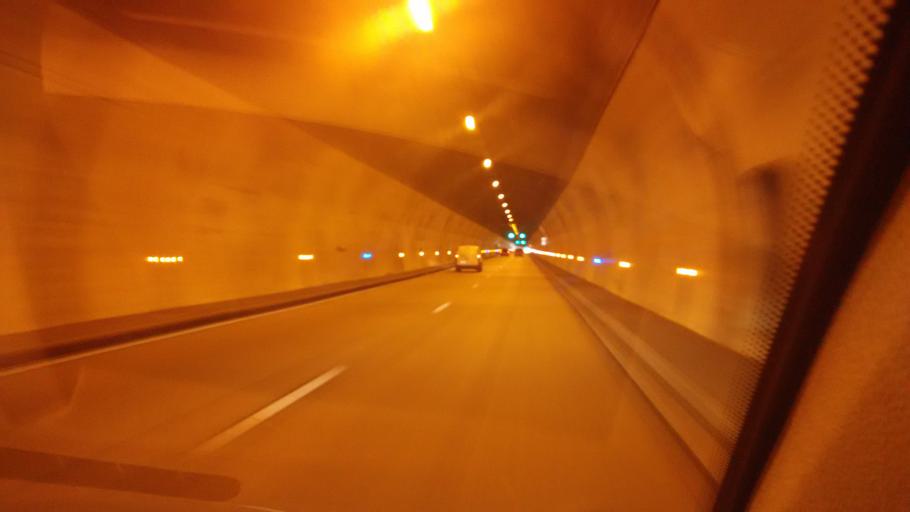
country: FR
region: Provence-Alpes-Cote d'Azur
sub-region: Departement des Alpes-Maritimes
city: Gorbio
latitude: 43.7719
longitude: 7.4502
